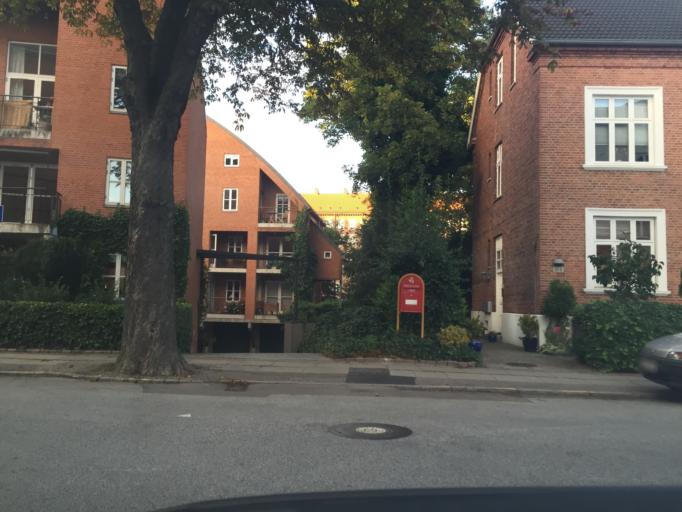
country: DK
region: Capital Region
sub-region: Frederiksberg Kommune
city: Frederiksberg
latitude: 55.6883
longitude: 12.5393
